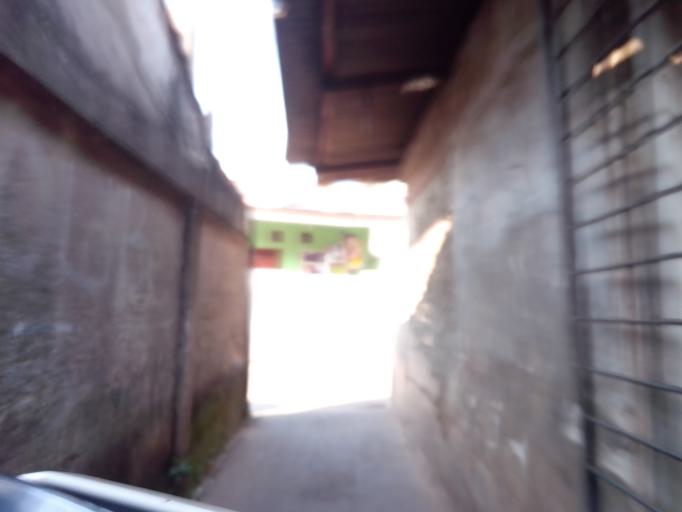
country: ID
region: Jakarta Raya
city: Jakarta
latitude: -6.2658
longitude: 106.8115
